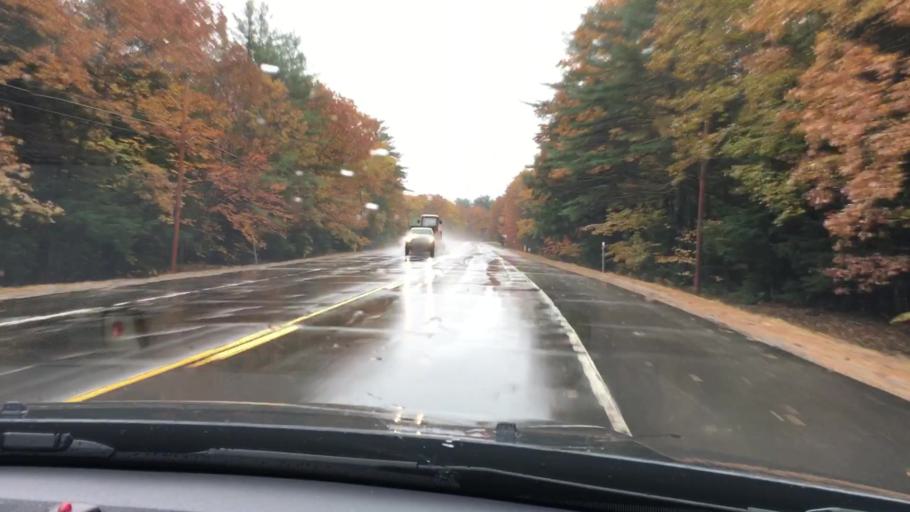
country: US
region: New Hampshire
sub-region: Grafton County
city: Ashland
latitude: 43.7162
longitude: -71.6247
